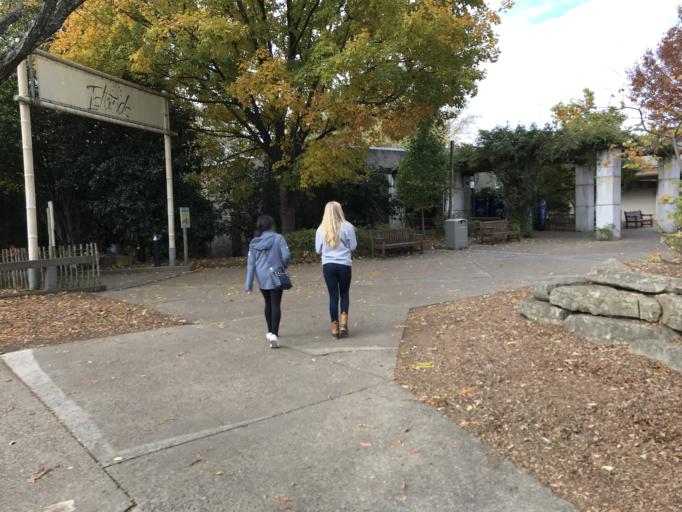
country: US
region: Kentucky
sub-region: Jefferson County
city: Audubon Park
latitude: 38.2052
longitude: -85.7069
